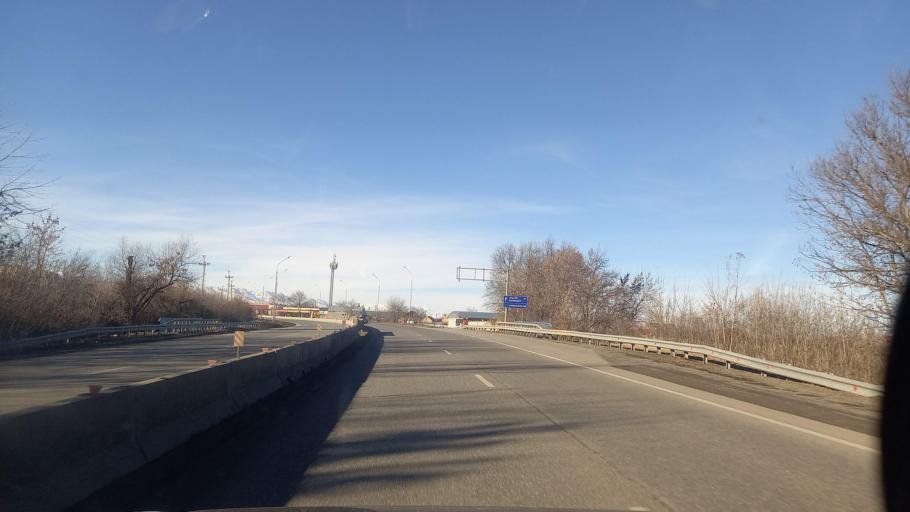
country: RU
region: North Ossetia
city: Gizel'
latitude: 43.0290
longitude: 44.5817
